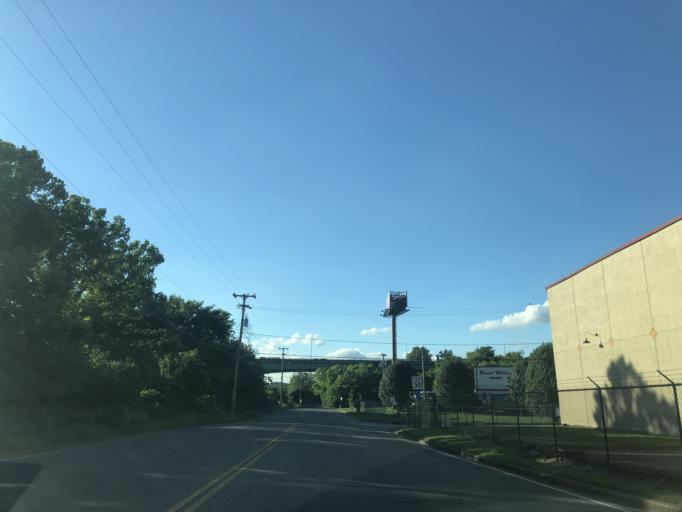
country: US
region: Tennessee
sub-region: Davidson County
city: Nashville
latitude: 36.1897
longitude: -86.7810
